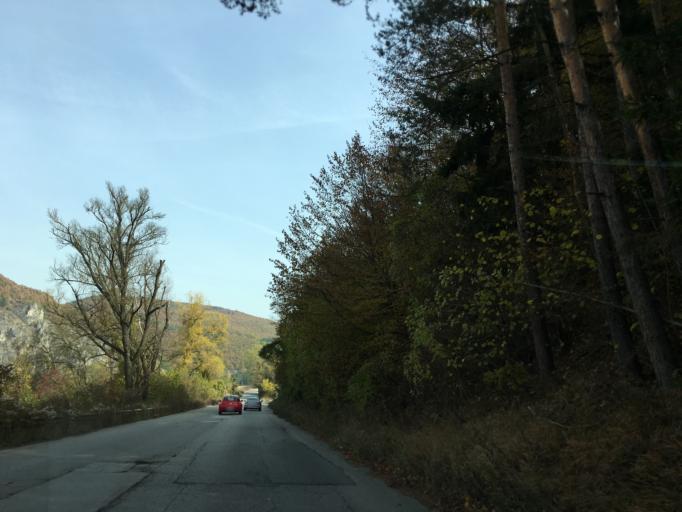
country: BG
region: Sofiya
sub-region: Obshtina Elin Pelin
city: Elin Pelin
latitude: 42.5340
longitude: 23.5105
